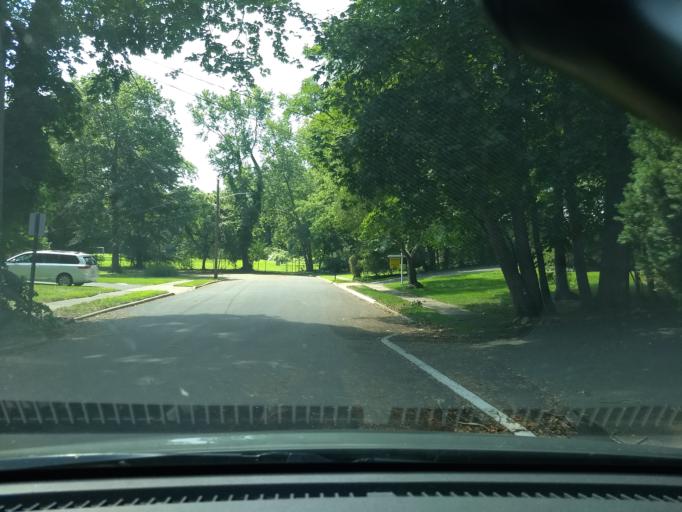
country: US
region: New Jersey
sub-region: Bergen County
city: Ridgewood
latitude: 40.9760
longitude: -74.1091
